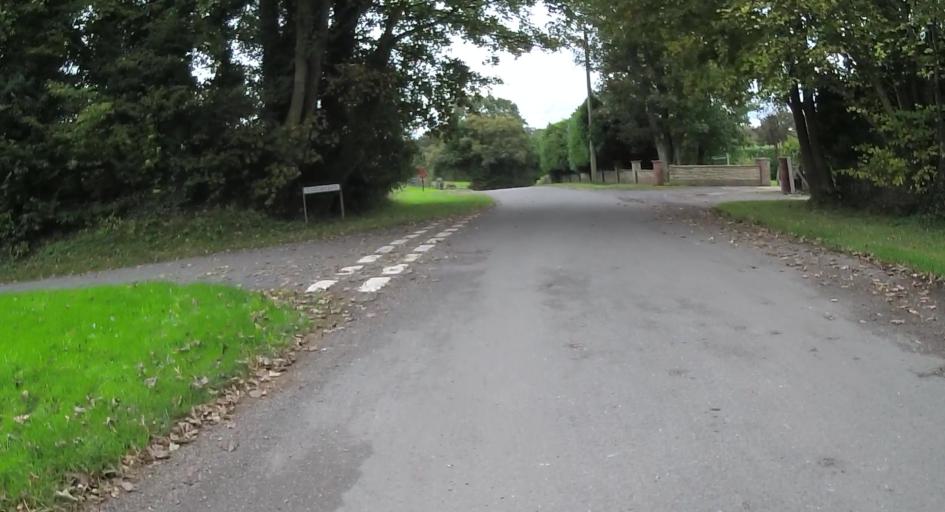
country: GB
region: England
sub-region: Hampshire
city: Four Marks
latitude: 51.1166
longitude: -1.0786
